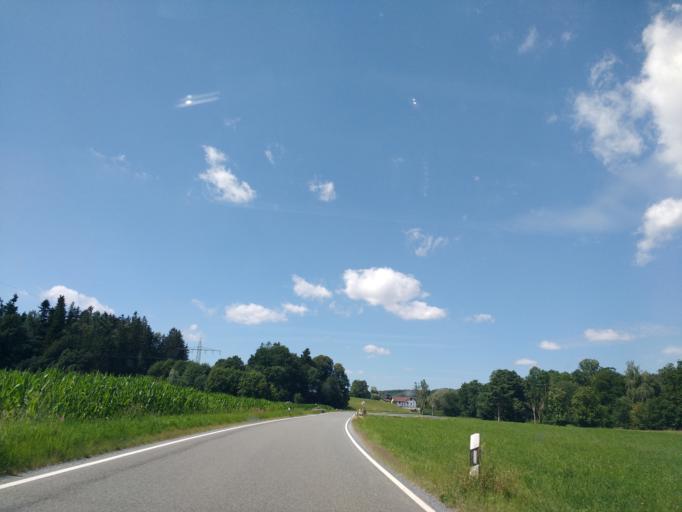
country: DE
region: Bavaria
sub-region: Upper Bavaria
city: Taufkirchen
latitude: 48.1333
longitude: 12.4400
